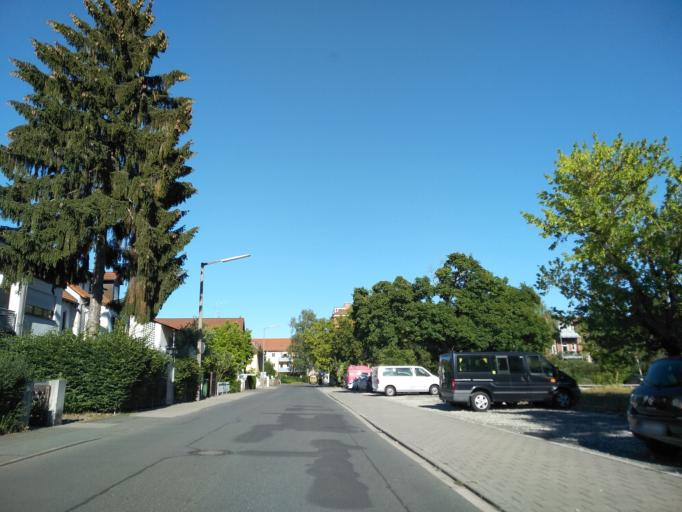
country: DE
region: Bavaria
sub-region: Regierungsbezirk Mittelfranken
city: Erlangen
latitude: 49.5980
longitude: 11.0279
